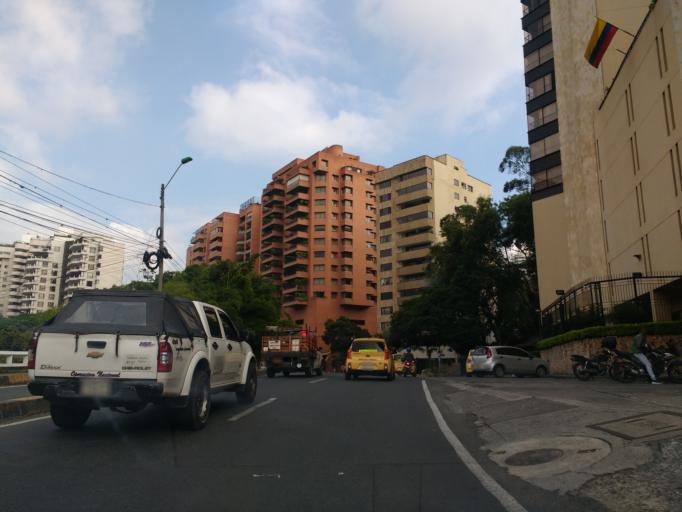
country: CO
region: Valle del Cauca
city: Cali
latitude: 3.4516
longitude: -76.5409
